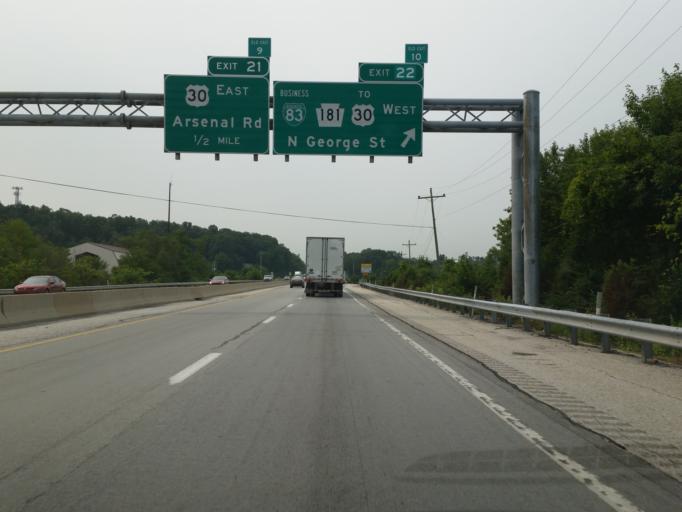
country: US
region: Pennsylvania
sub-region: York County
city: North York
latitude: 39.9953
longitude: -76.7356
